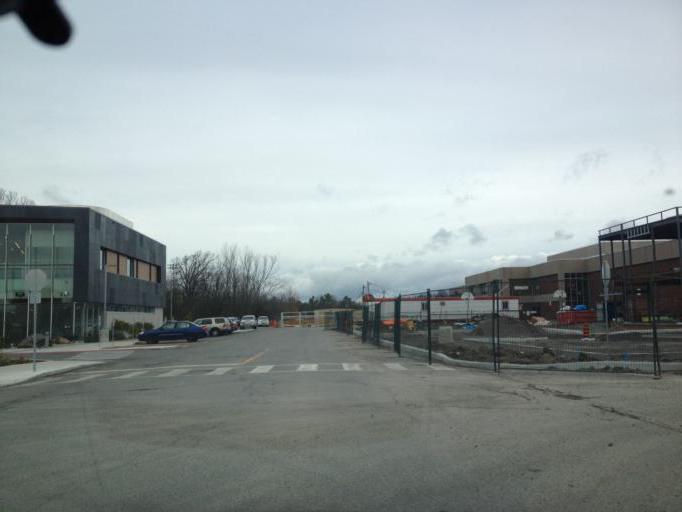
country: CA
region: Ontario
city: Bells Corners
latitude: 45.3217
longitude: -75.8944
